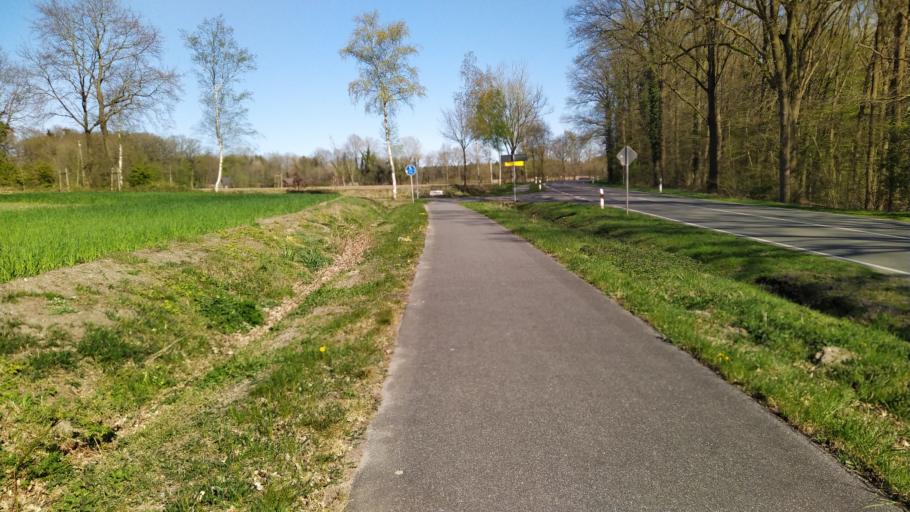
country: DE
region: Lower Saxony
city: Klein Meckelsen
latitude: 53.2989
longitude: 9.4086
